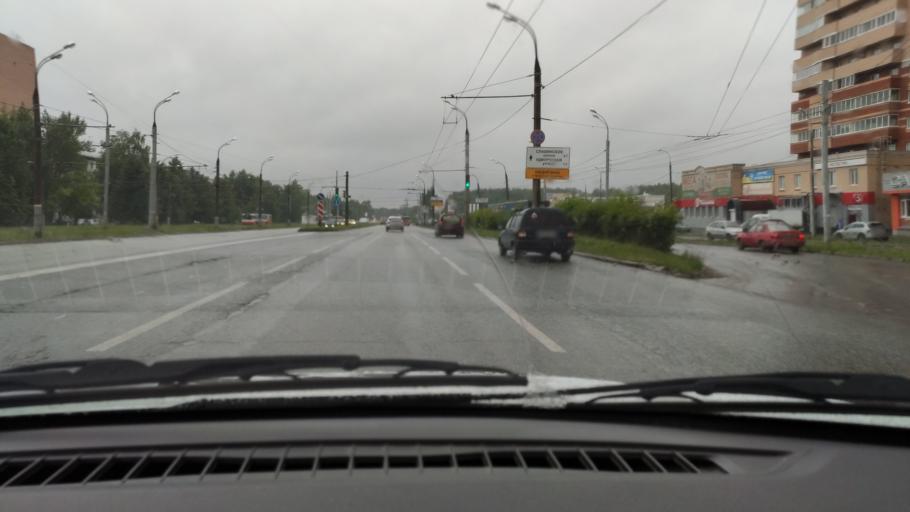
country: RU
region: Udmurtiya
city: Izhevsk
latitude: 56.8881
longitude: 53.2425
